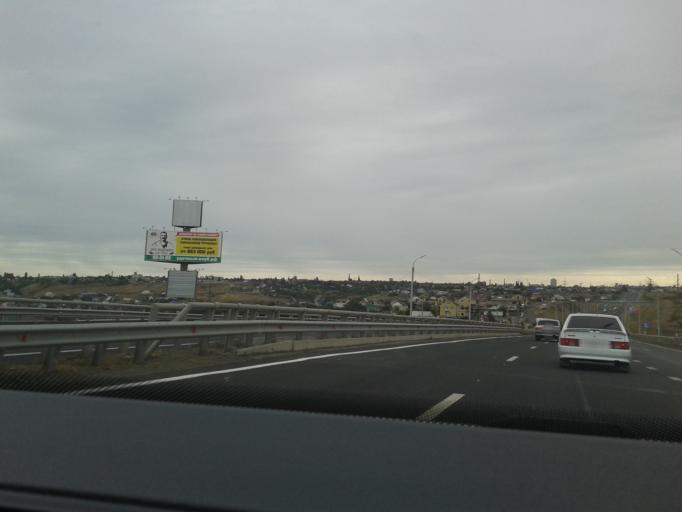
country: RU
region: Volgograd
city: Gorodishche
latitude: 48.7991
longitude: 44.4554
